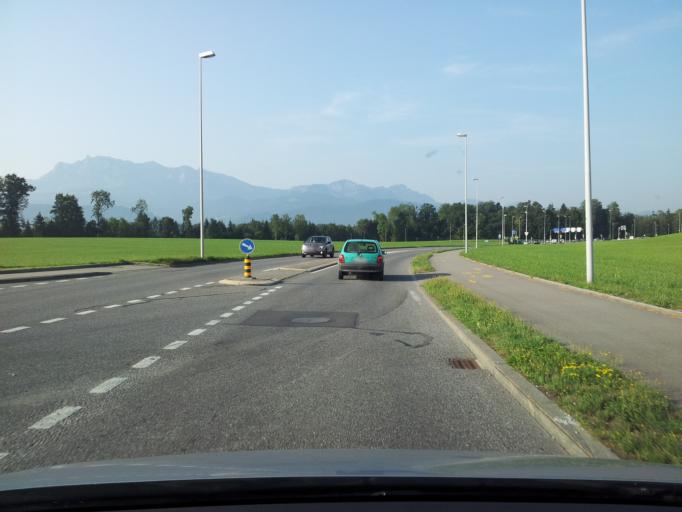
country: CH
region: Lucerne
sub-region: Hochdorf District
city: Emmen
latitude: 47.0855
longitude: 8.2494
